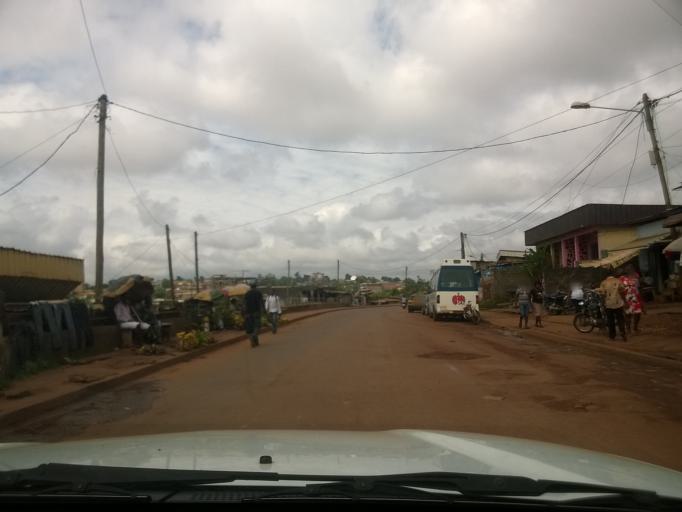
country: CM
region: Centre
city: Yaounde
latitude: 3.8717
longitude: 11.5400
